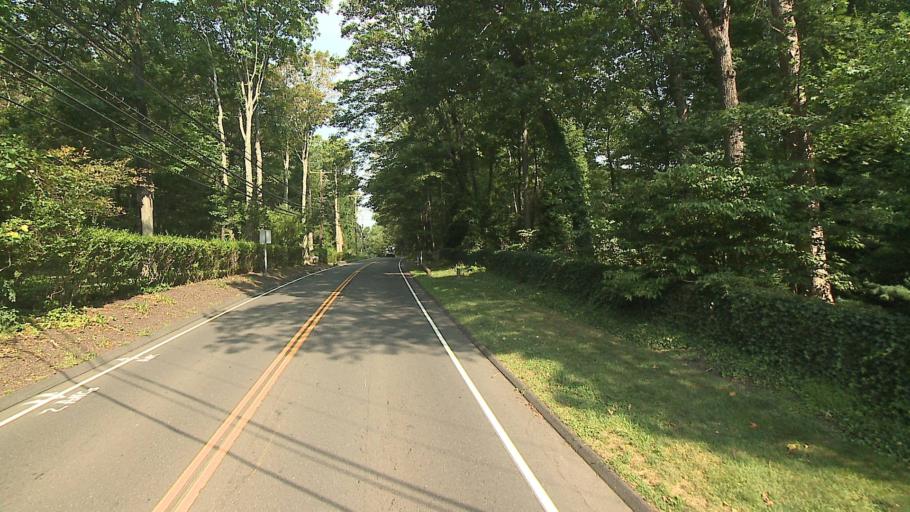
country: US
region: Connecticut
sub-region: Fairfield County
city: Wilton
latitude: 41.2050
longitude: -73.3836
